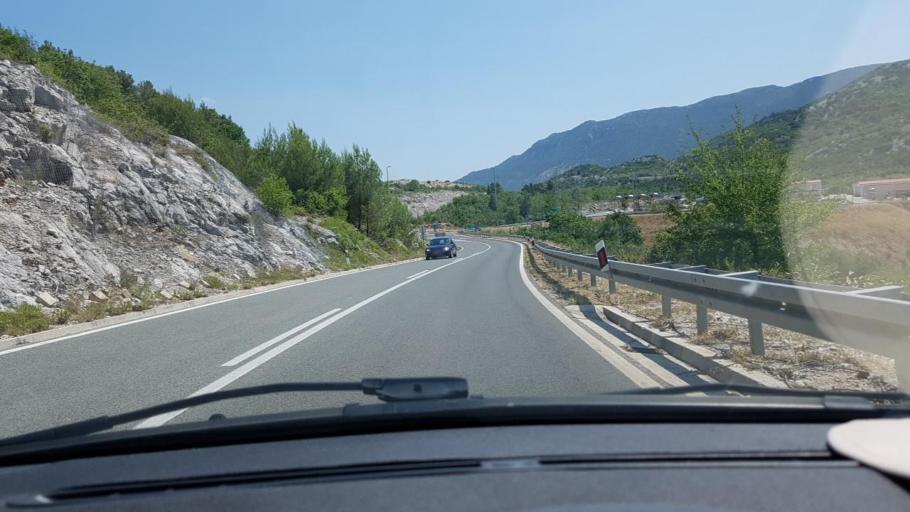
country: HR
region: Splitsko-Dalmatinska
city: Vrgorac
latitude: 43.1951
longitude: 17.3787
